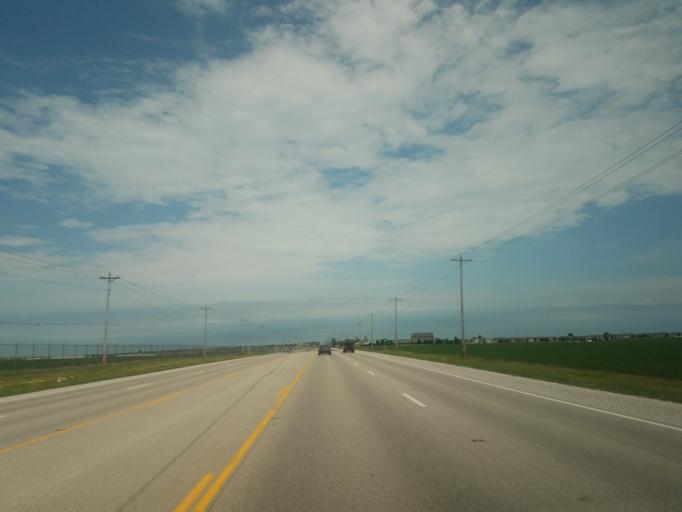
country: US
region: Illinois
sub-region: McLean County
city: Downs
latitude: 40.4815
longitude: -88.9024
